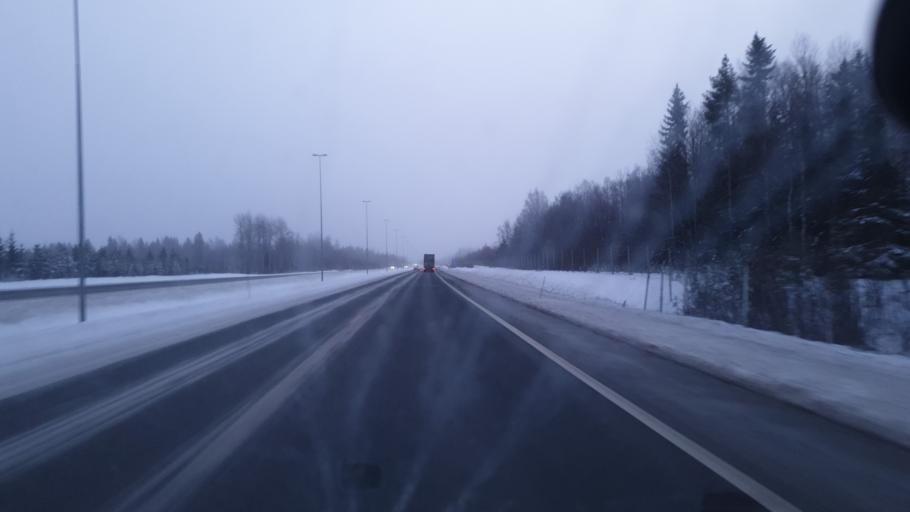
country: FI
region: Lapland
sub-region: Kemi-Tornio
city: Keminmaa
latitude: 65.8340
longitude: 24.3501
